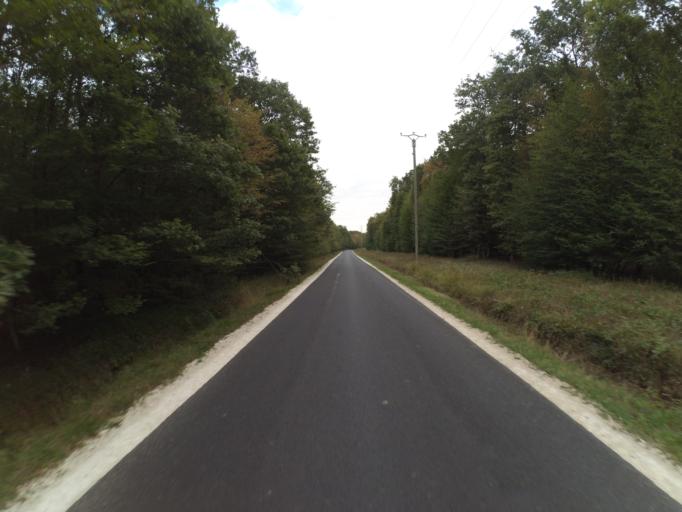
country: FR
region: Centre
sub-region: Departement d'Indre-et-Loire
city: Auzouer-en-Touraine
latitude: 47.5098
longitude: 0.9793
